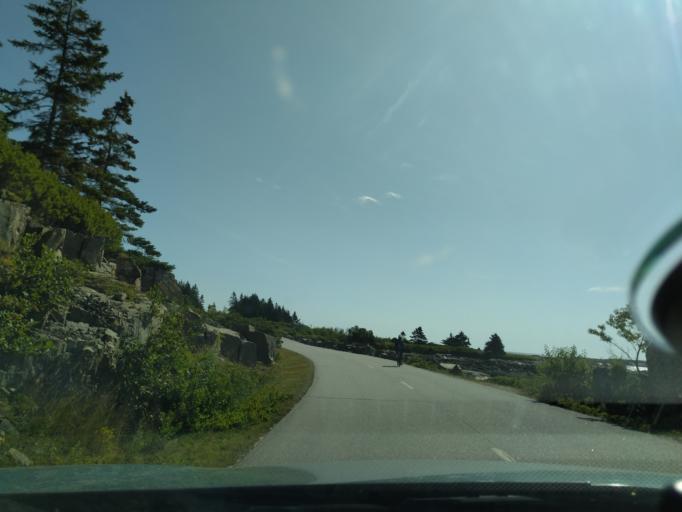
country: US
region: Maine
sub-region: Hancock County
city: Gouldsboro
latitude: 44.3384
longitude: -68.0481
